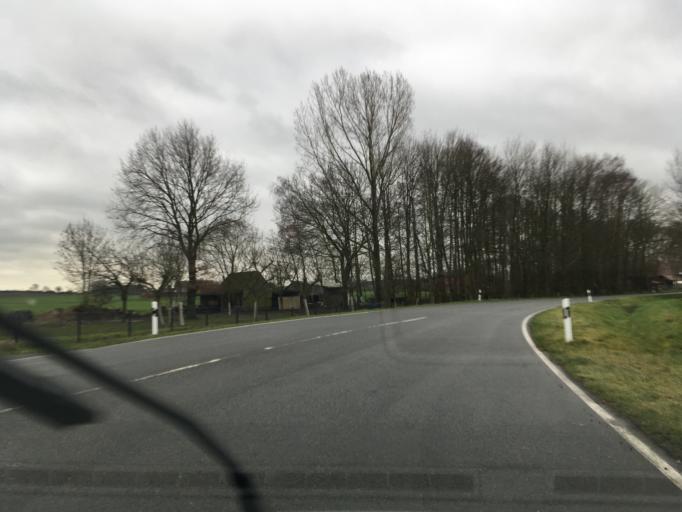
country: DE
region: North Rhine-Westphalia
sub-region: Regierungsbezirk Munster
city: Schoppingen
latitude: 52.0978
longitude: 7.1745
